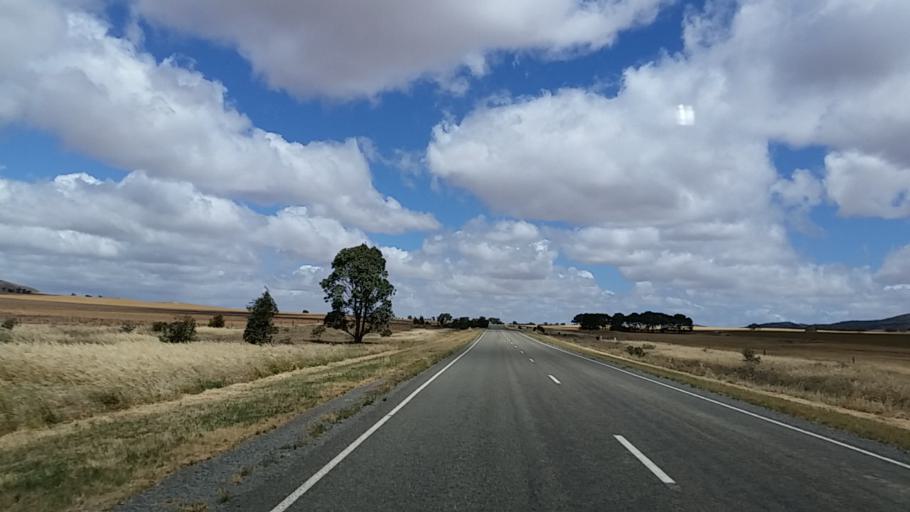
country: AU
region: South Australia
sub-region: Peterborough
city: Peterborough
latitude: -32.8620
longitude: 138.5415
